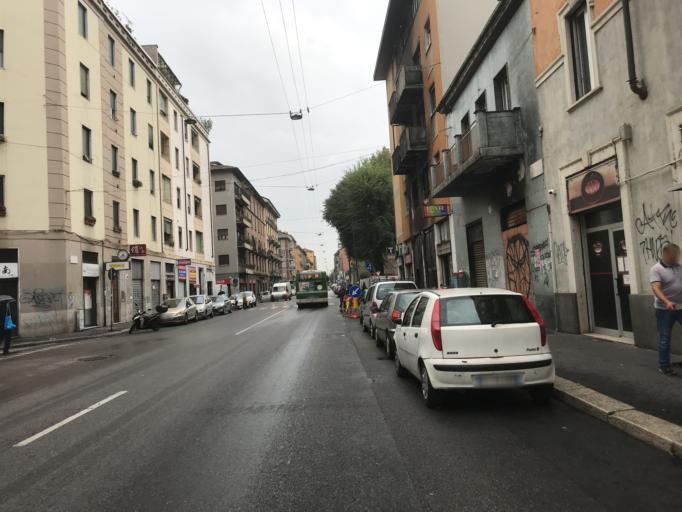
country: IT
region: Lombardy
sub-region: Citta metropolitana di Milano
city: Sesto San Giovanni
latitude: 45.4942
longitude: 9.2272
